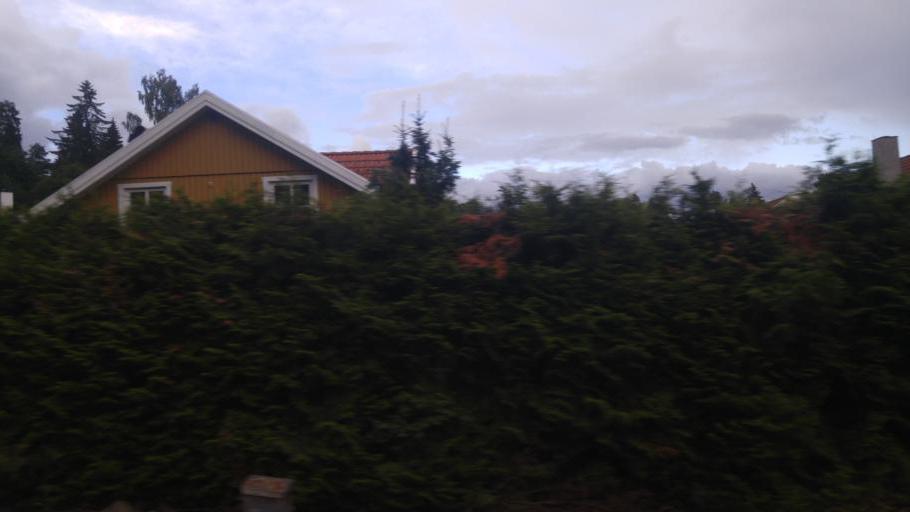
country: NO
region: Oslo
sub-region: Oslo
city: Sjolyststranda
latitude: 59.9558
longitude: 10.7016
